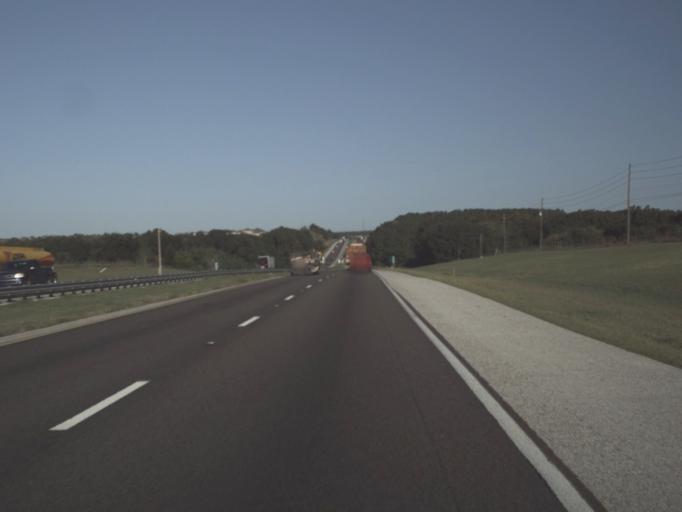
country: US
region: Florida
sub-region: Lake County
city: Montverde
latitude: 28.5633
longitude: -81.6853
